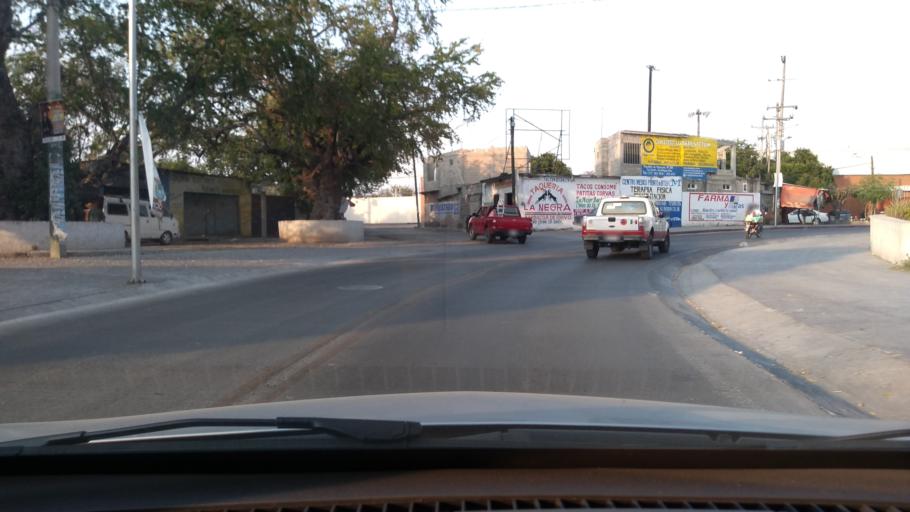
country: MX
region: Morelos
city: Puente de Ixtla
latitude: 18.6327
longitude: -99.3239
